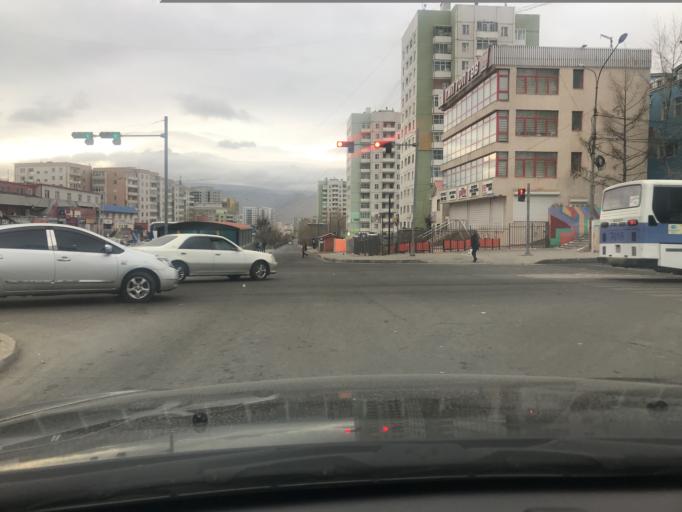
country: MN
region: Ulaanbaatar
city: Ulaanbaatar
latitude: 47.9244
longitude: 106.9416
